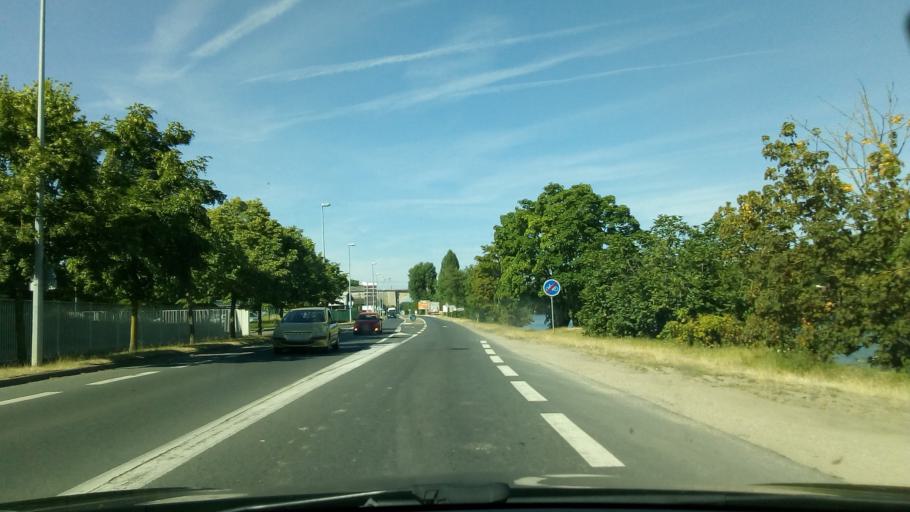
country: FR
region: Ile-de-France
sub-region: Departement de Seine-et-Marne
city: Le Mee-sur-Seine
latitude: 48.5345
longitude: 2.6456
